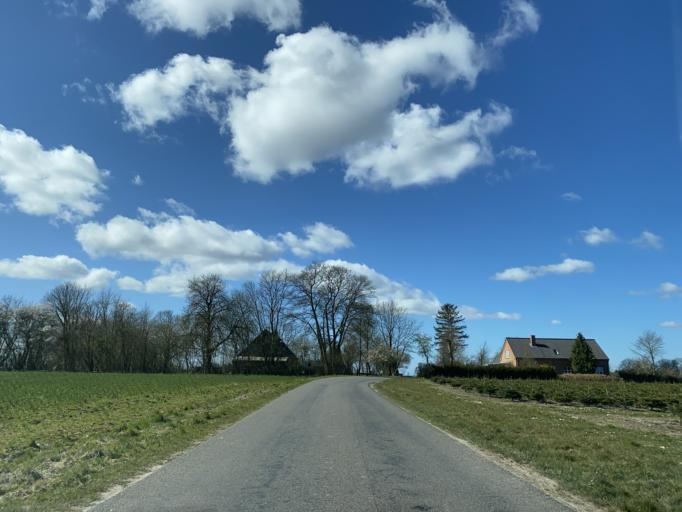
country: DK
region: Central Jutland
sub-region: Favrskov Kommune
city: Ulstrup
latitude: 56.3431
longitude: 9.8135
